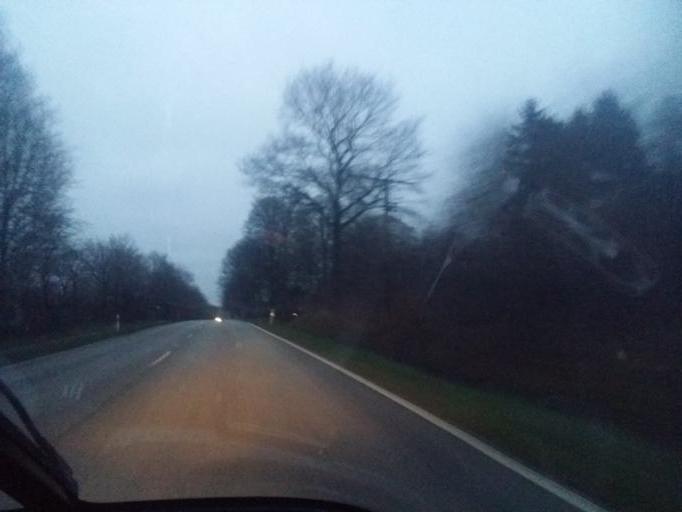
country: DE
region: Schleswig-Holstein
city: Warringholz
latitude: 54.0730
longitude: 9.4659
